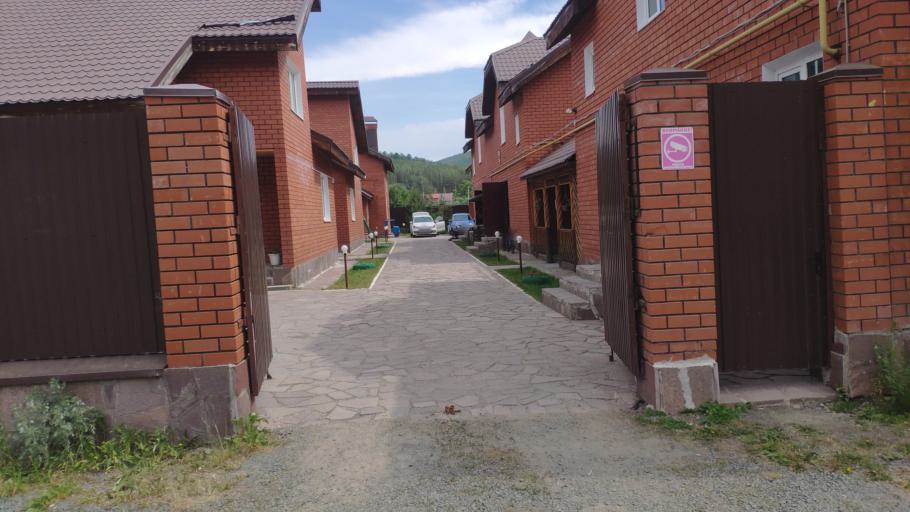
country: RU
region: Bashkortostan
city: Abzakovo
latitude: 53.8131
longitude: 58.6351
